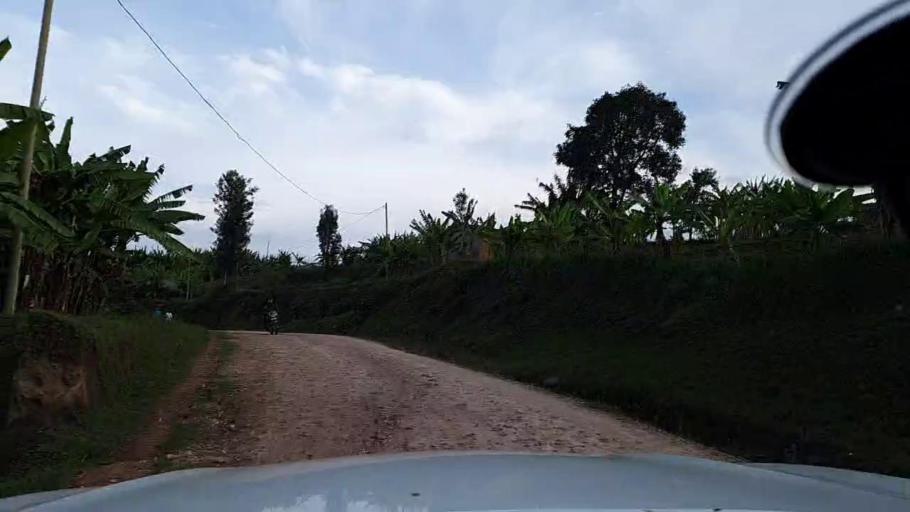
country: RW
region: Southern Province
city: Gitarama
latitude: -2.2100
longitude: 29.6070
